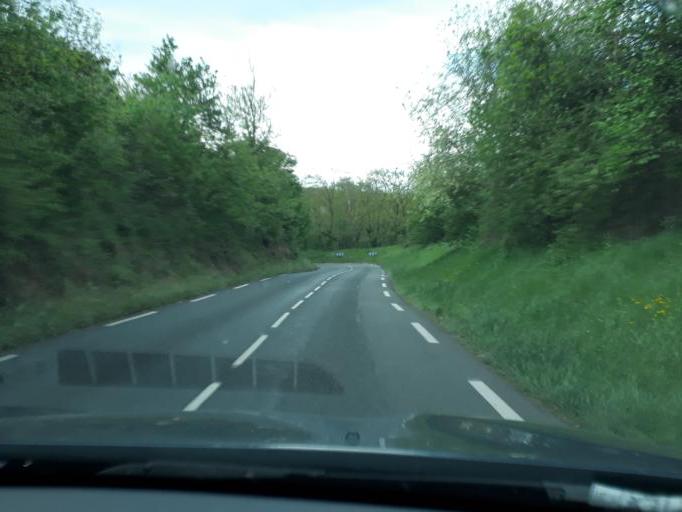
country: FR
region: Rhone-Alpes
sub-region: Departement du Rhone
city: Orlienas
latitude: 45.6763
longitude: 4.7245
